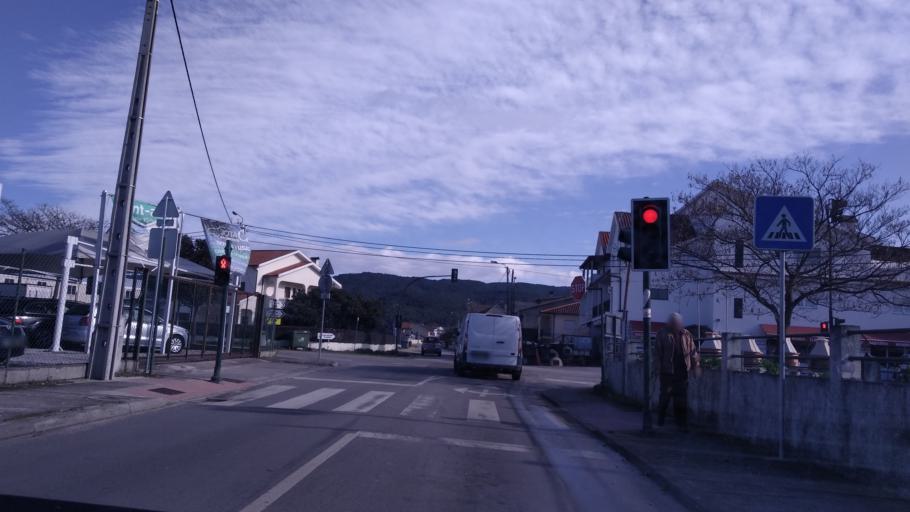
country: PT
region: Vila Real
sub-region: Chaves
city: Chaves
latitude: 41.7387
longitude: -7.4523
